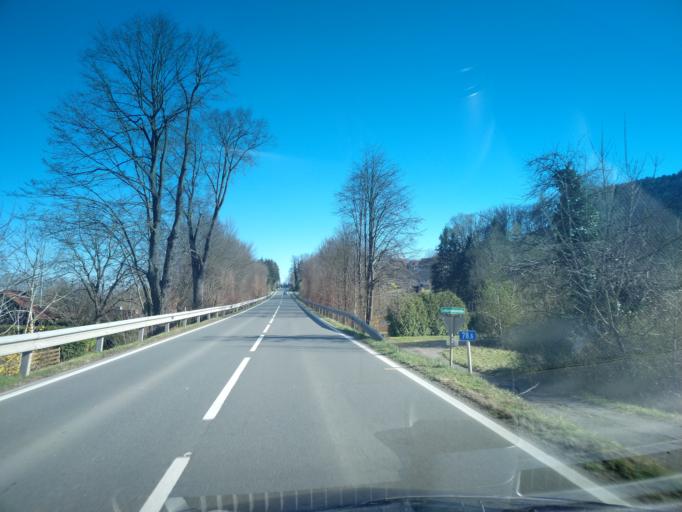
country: AT
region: Styria
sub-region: Politischer Bezirk Leibnitz
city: Wildon
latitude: 46.8824
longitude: 15.5218
